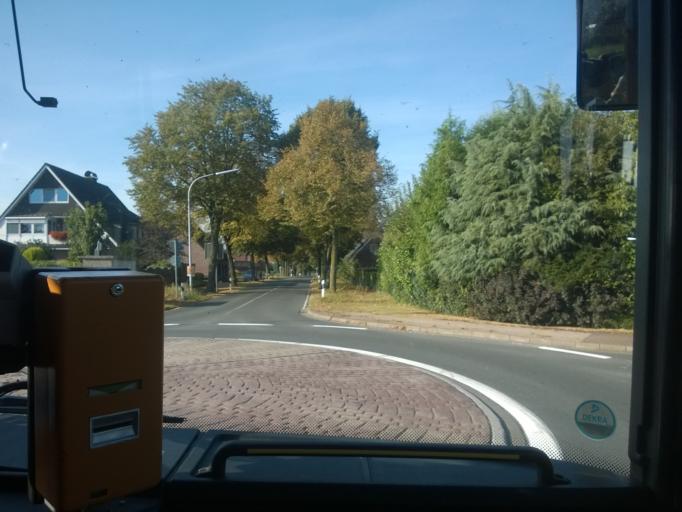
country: DE
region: North Rhine-Westphalia
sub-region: Regierungsbezirk Munster
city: Sudlohn
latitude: 51.9119
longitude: 6.8544
